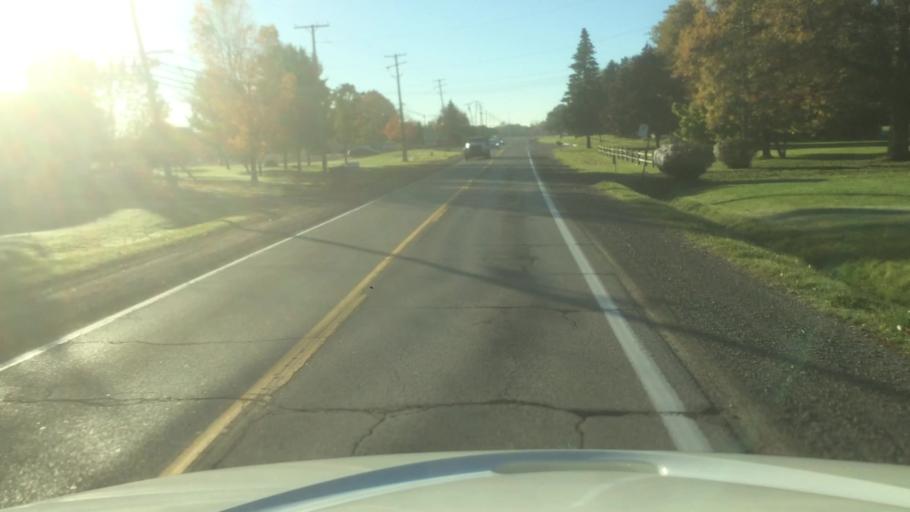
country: US
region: Michigan
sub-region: Macomb County
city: Shelby
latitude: 42.6778
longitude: -82.9442
